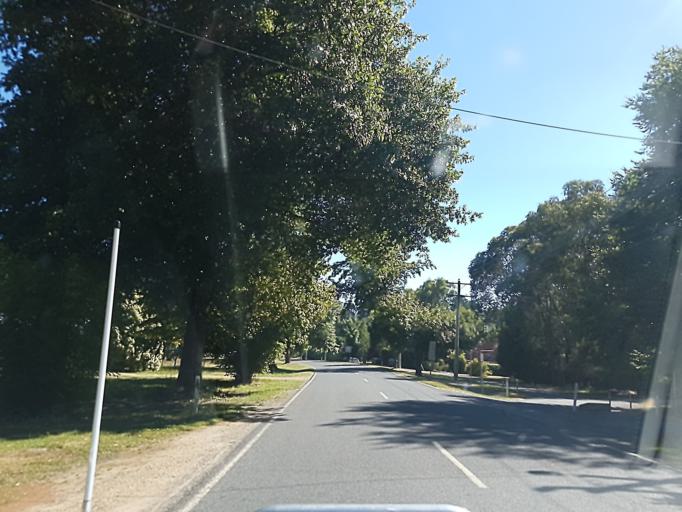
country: AU
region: Victoria
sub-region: Alpine
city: Mount Beauty
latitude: -36.8875
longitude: 147.0645
